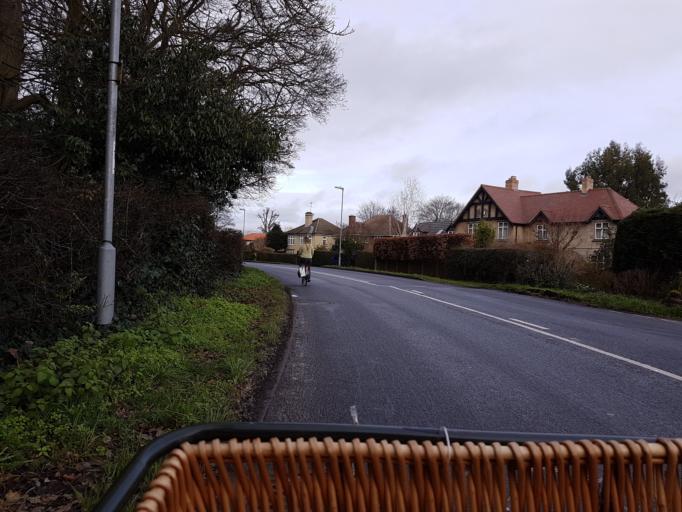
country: GB
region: England
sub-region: Cambridgeshire
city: Girton
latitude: 52.2273
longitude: 0.0877
